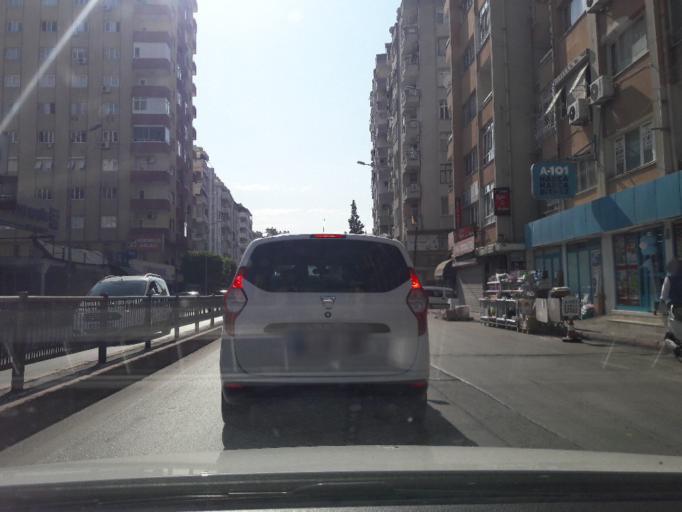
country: TR
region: Adana
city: Adana
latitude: 37.0111
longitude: 35.3233
